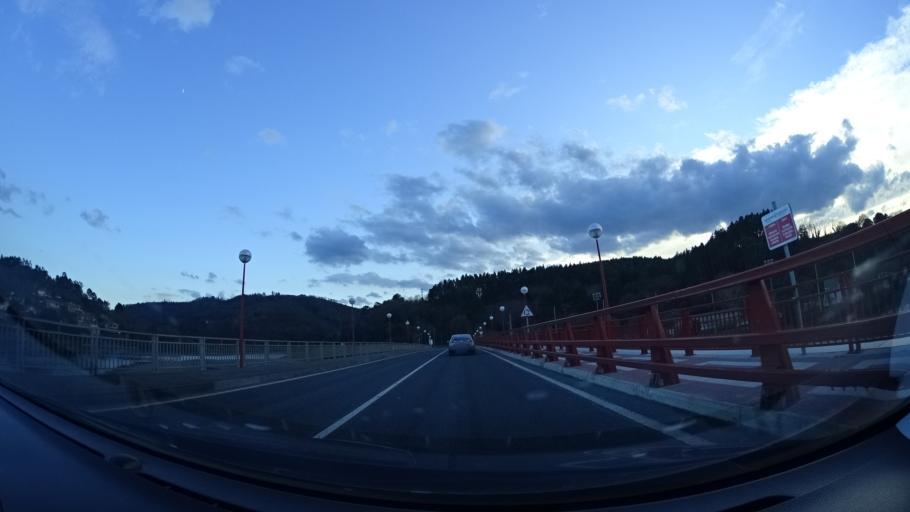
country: ES
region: Basque Country
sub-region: Bizkaia
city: Plentzia
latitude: 43.3987
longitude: -2.9439
